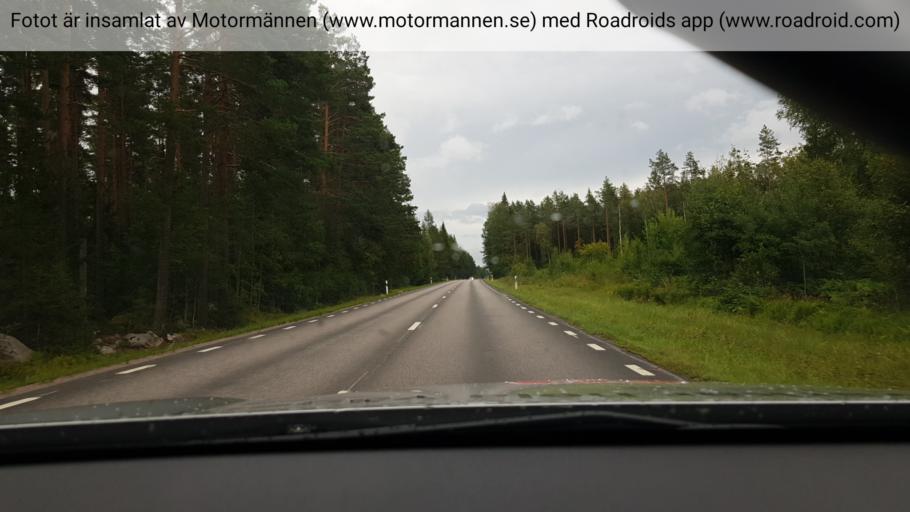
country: SE
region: Uppsala
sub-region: Alvkarleby Kommun
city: AElvkarleby
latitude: 60.5464
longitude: 17.5288
